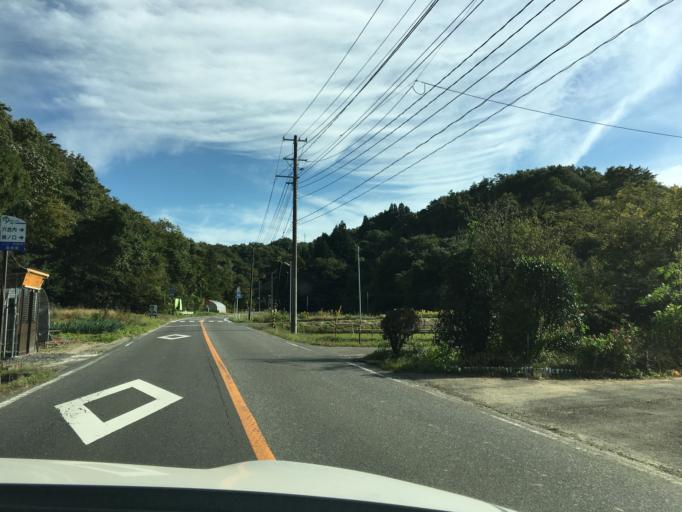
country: JP
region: Fukushima
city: Miharu
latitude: 37.3637
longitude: 140.4607
